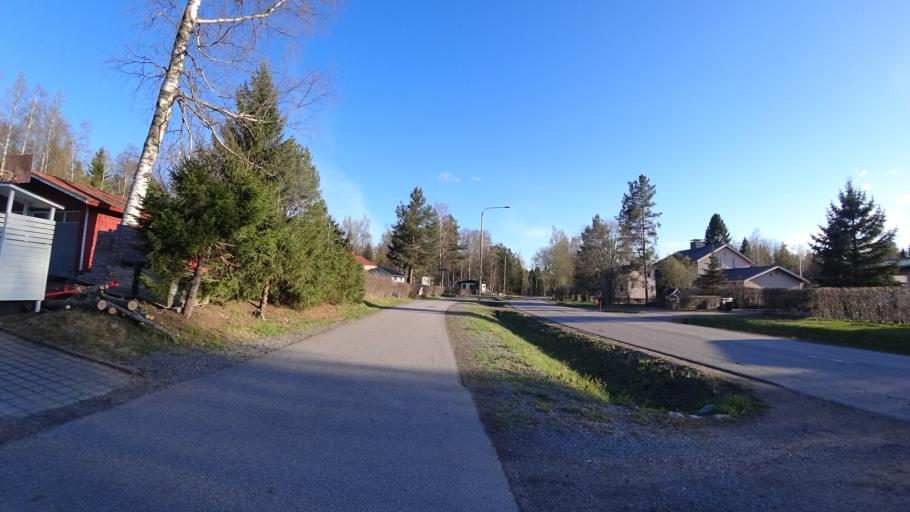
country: FI
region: Pirkanmaa
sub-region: Tampere
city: Yloejaervi
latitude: 61.5066
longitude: 23.5936
